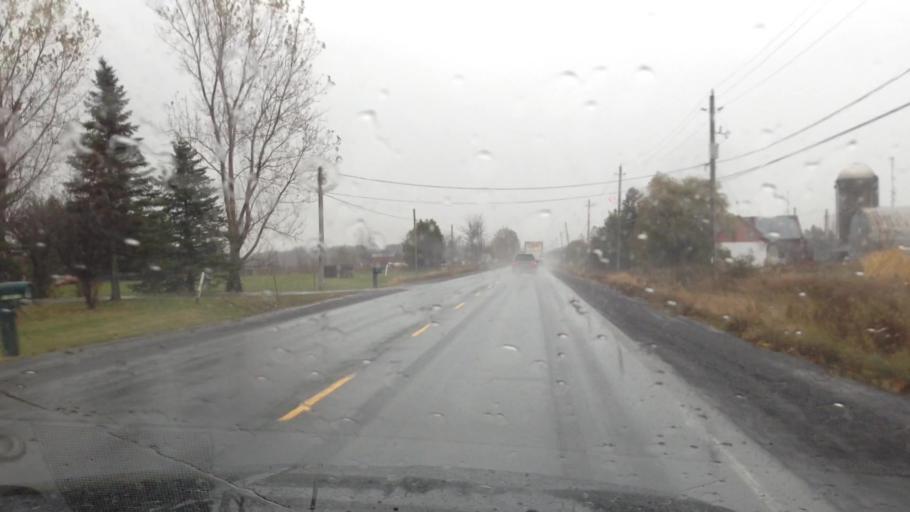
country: CA
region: Ontario
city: Bourget
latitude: 45.2849
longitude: -75.3195
